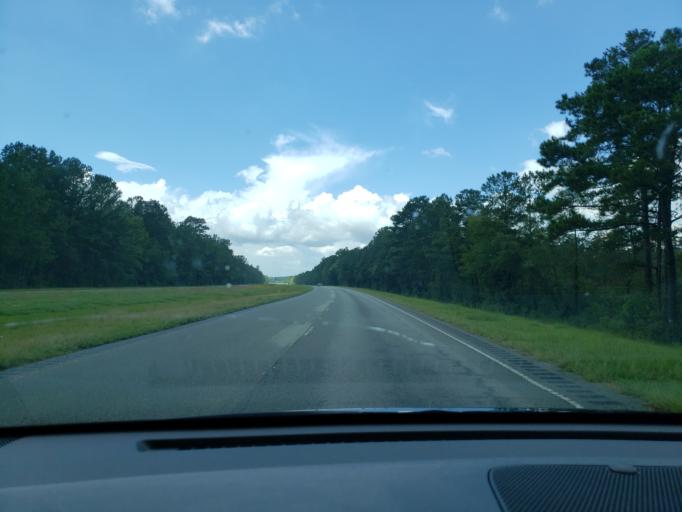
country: US
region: North Carolina
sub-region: Bladen County
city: Elizabethtown
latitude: 34.6345
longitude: -78.6595
